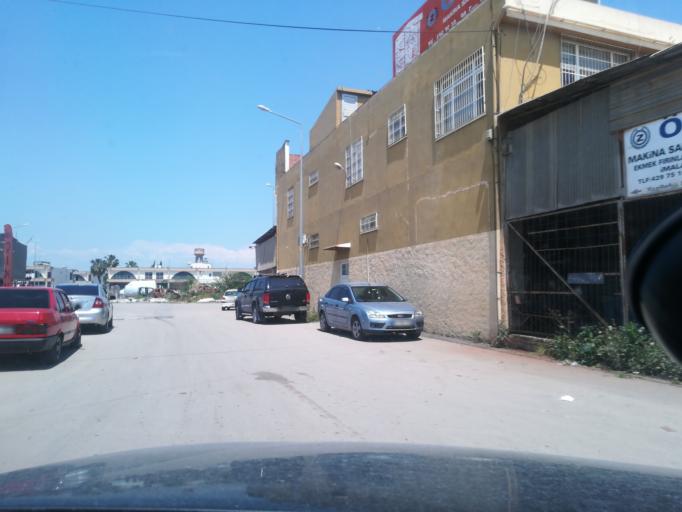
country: TR
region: Adana
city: Seyhan
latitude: 36.9901
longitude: 35.2546
